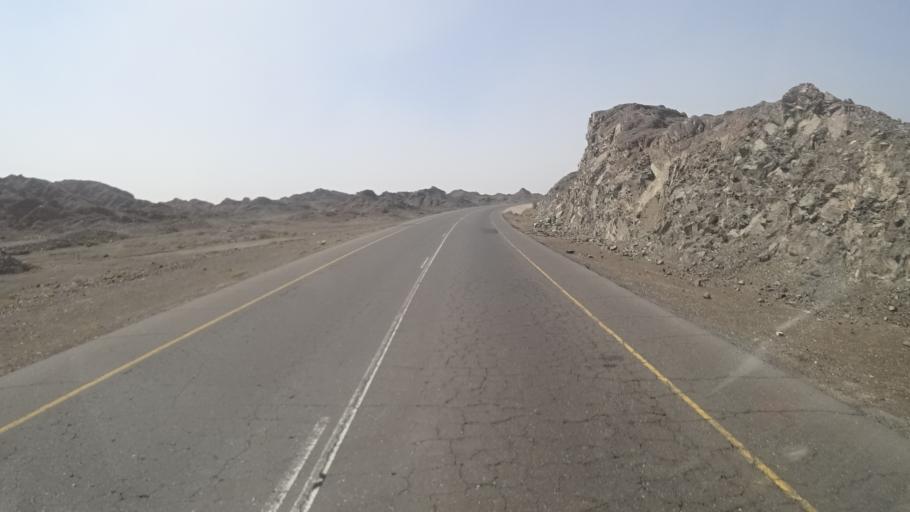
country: OM
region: Ash Sharqiyah
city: Ibra'
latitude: 22.6211
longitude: 58.3098
